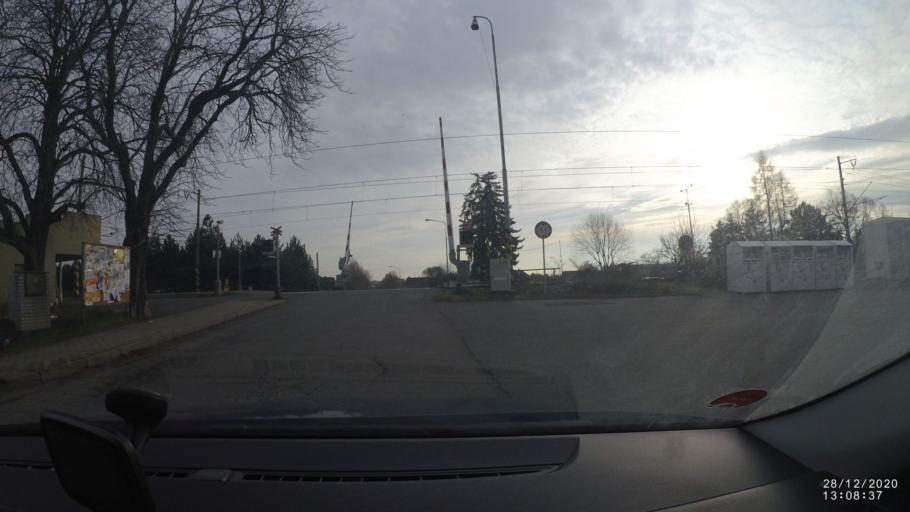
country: CZ
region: Central Bohemia
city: Zelenec
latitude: 50.1304
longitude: 14.6643
